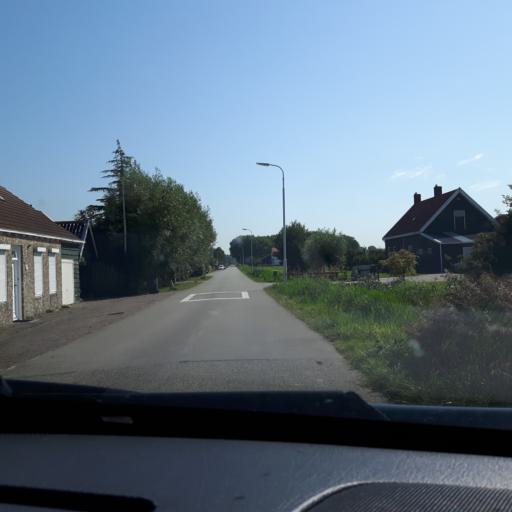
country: NL
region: Zeeland
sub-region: Gemeente Goes
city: Goes
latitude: 51.4995
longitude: 3.8120
